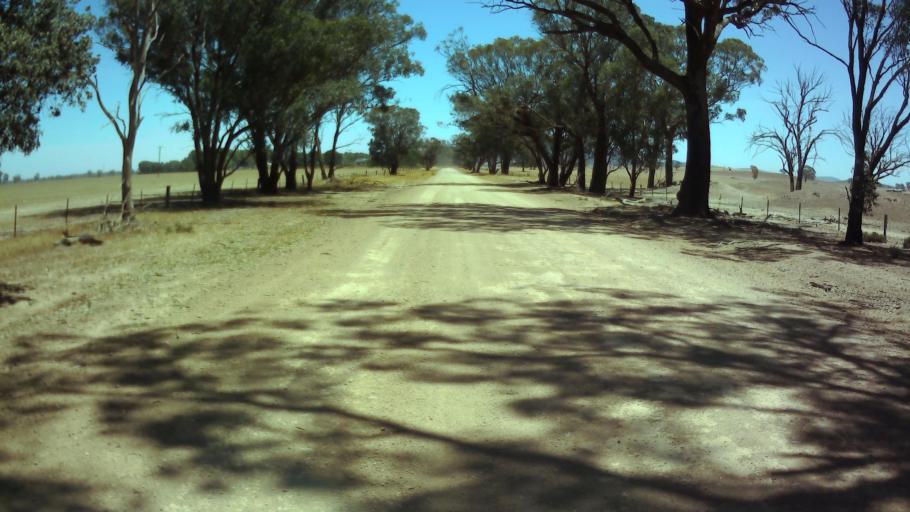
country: AU
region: New South Wales
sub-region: Weddin
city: Grenfell
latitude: -34.0118
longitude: 148.1766
